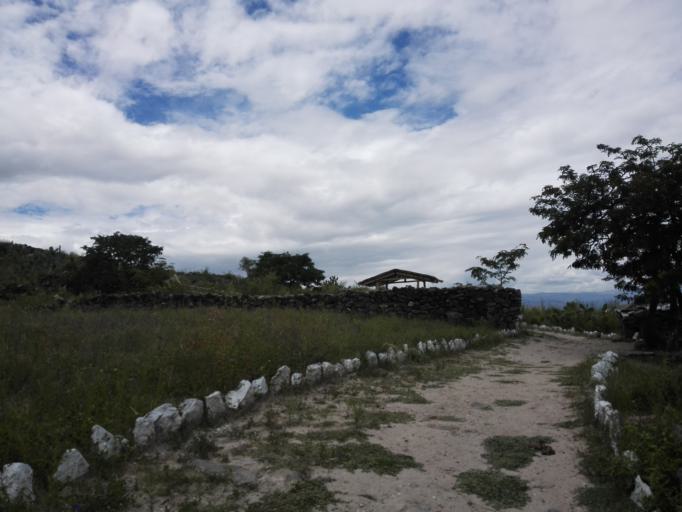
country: PE
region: Ayacucho
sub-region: Provincia de Huamanga
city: Pacaycasa
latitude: -13.0623
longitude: -74.1967
